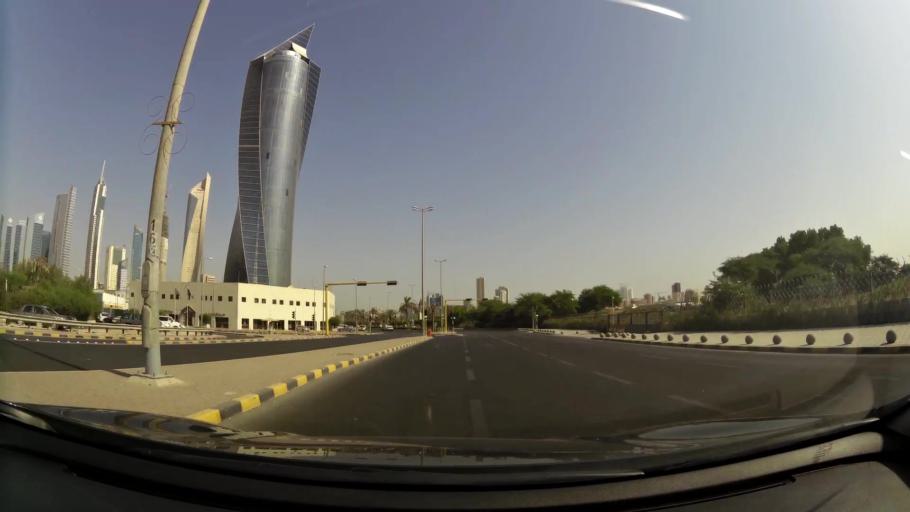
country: KW
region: Al Asimah
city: Ad Dasmah
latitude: 29.3679
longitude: 47.9916
